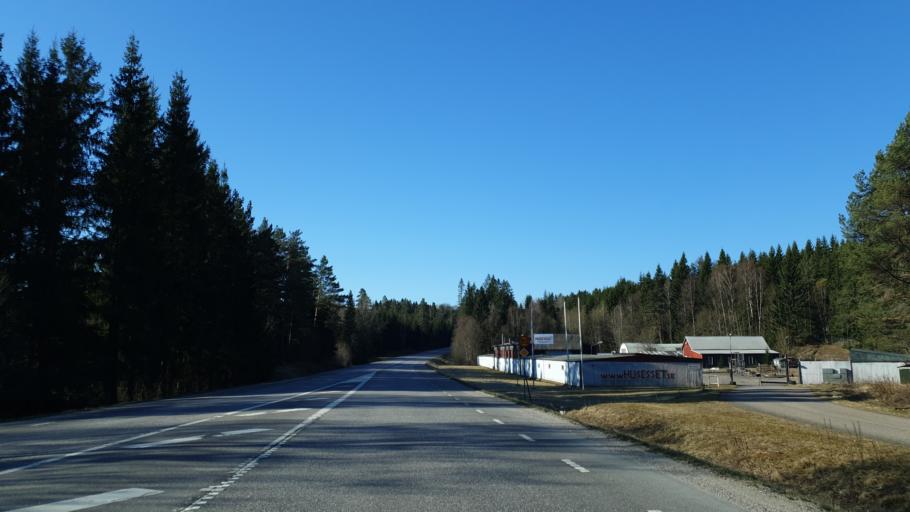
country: SE
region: Vaestra Goetaland
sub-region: Boras Kommun
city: Dalsjofors
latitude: 57.7626
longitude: 13.1137
